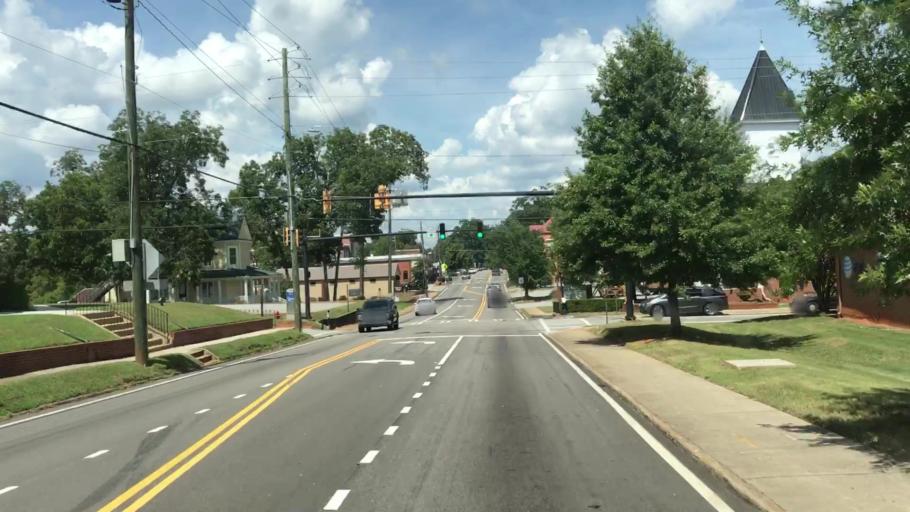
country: US
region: Georgia
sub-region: Oconee County
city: Watkinsville
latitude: 33.8619
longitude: -83.4081
